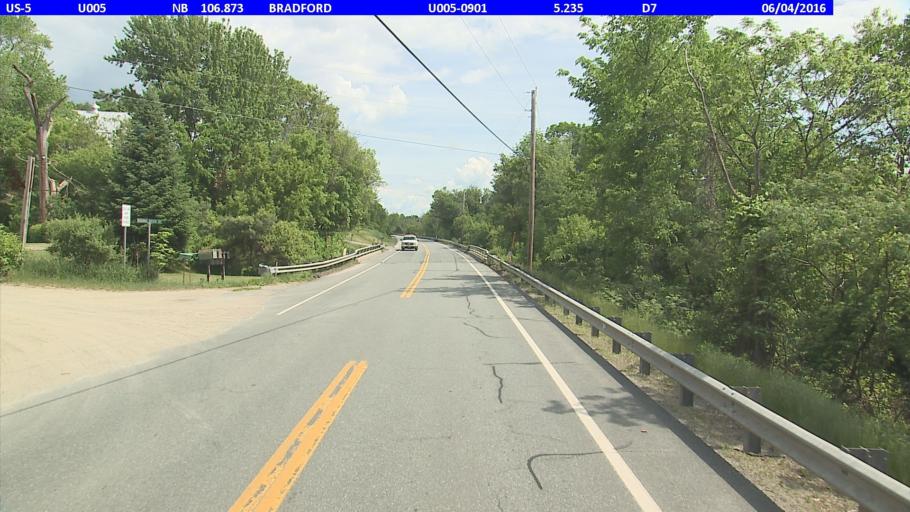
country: US
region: New Hampshire
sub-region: Grafton County
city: Haverhill
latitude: 44.0244
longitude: -72.0941
